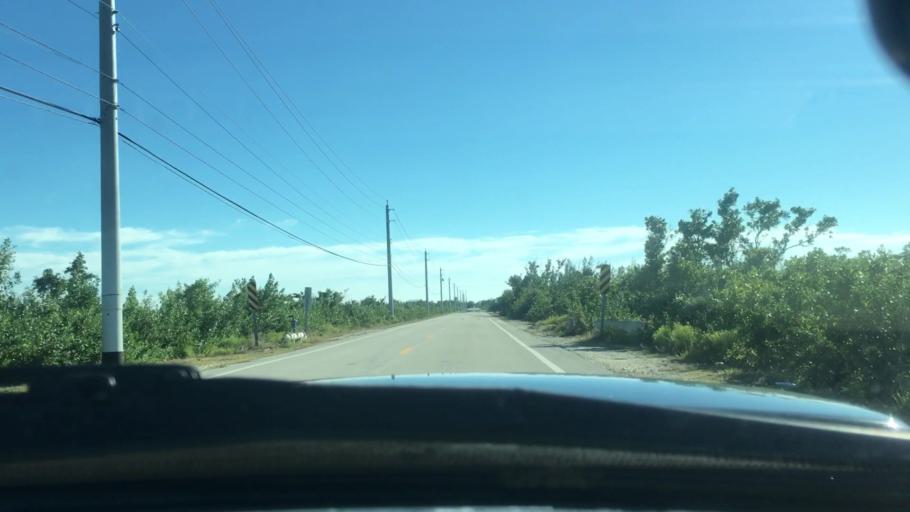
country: US
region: Florida
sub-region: Monroe County
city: Cudjoe Key
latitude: 24.6746
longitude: -81.4997
